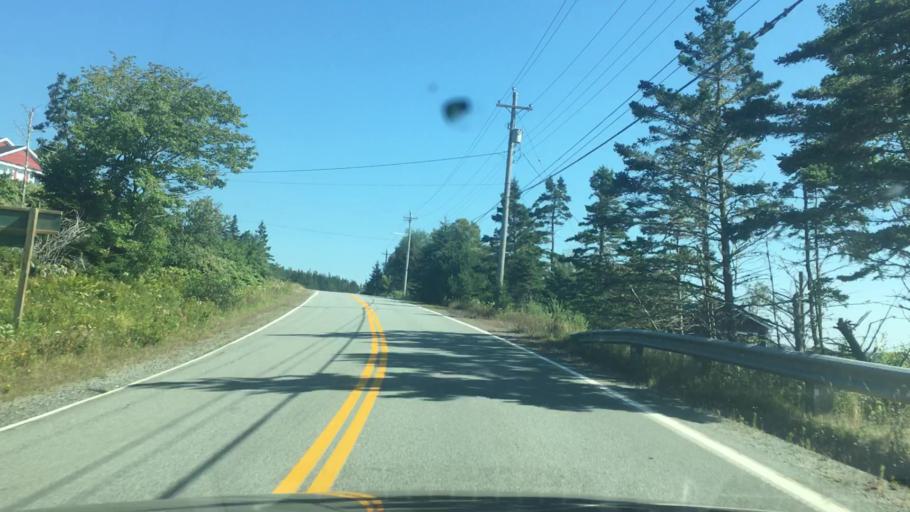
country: CA
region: Nova Scotia
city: New Glasgow
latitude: 44.8239
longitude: -62.6309
